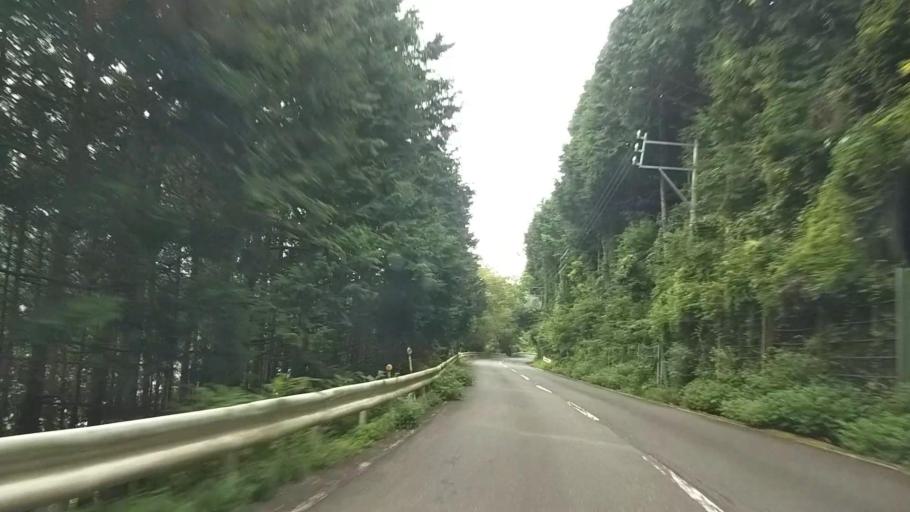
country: JP
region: Shizuoka
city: Fujinomiya
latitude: 35.2103
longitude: 138.5419
